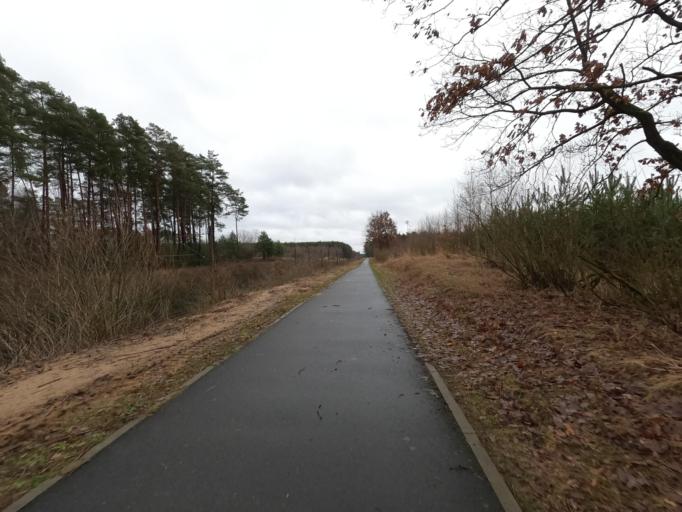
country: PL
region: Greater Poland Voivodeship
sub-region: Powiat pilski
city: Kaczory
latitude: 53.1226
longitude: 16.8202
